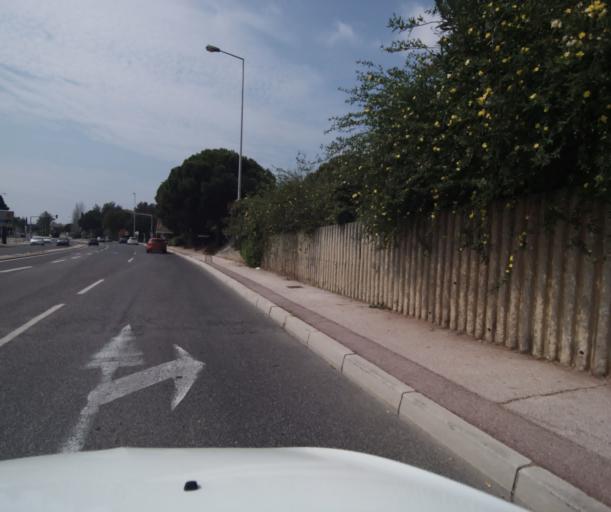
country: FR
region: Provence-Alpes-Cote d'Azur
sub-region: Departement du Var
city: La Garde
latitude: 43.1338
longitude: 6.0179
